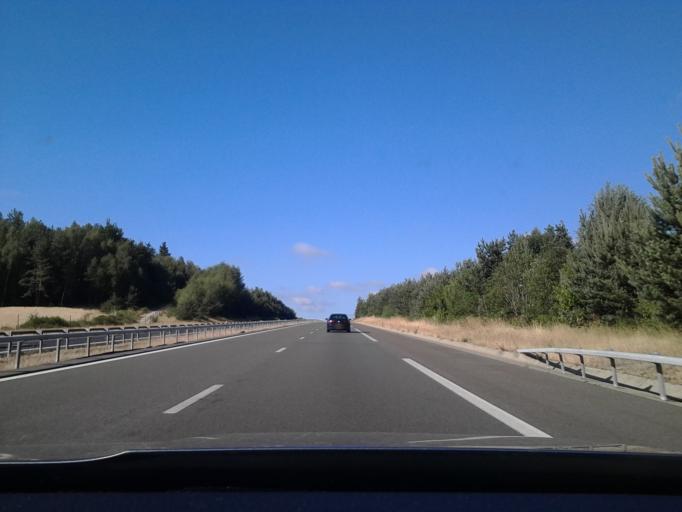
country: FR
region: Languedoc-Roussillon
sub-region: Departement de la Lozere
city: Aumont-Aubrac
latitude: 44.6548
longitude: 3.2527
